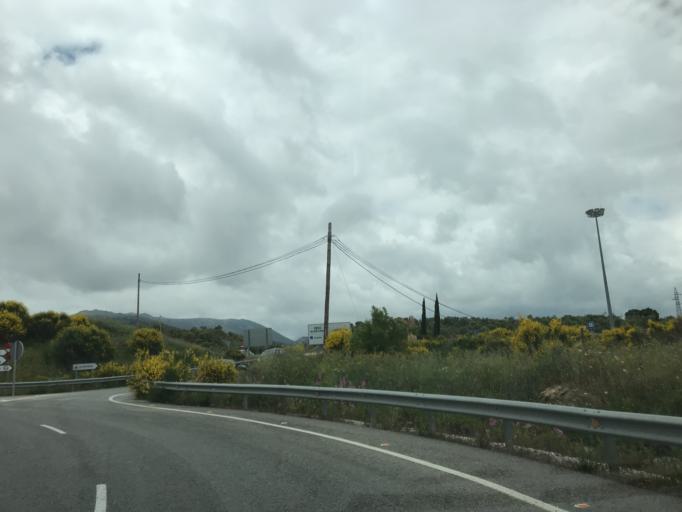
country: ES
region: Andalusia
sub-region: Provincia de Malaga
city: Ronda
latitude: 36.7264
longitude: -5.1469
